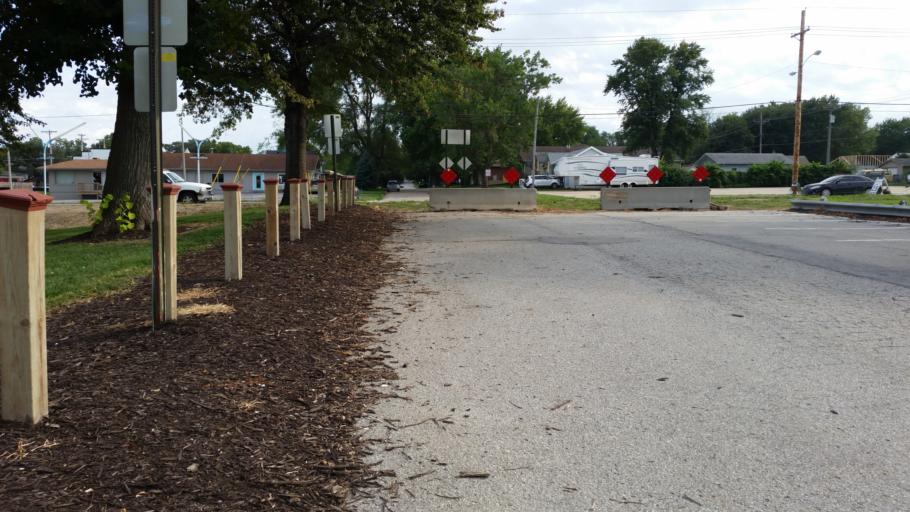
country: US
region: Nebraska
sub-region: Sarpy County
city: Papillion
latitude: 41.1548
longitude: -96.0443
